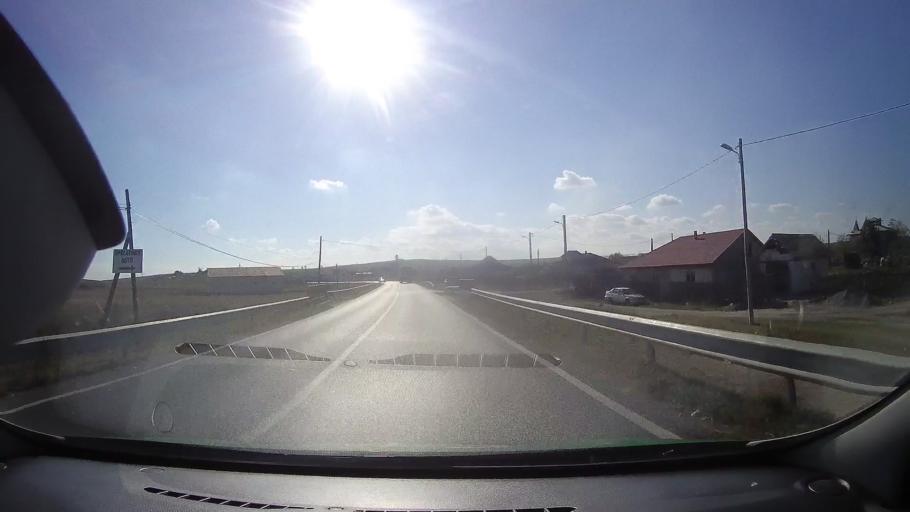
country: RO
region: Tulcea
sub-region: Comuna Baia
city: Baia
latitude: 44.7225
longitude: 28.6794
